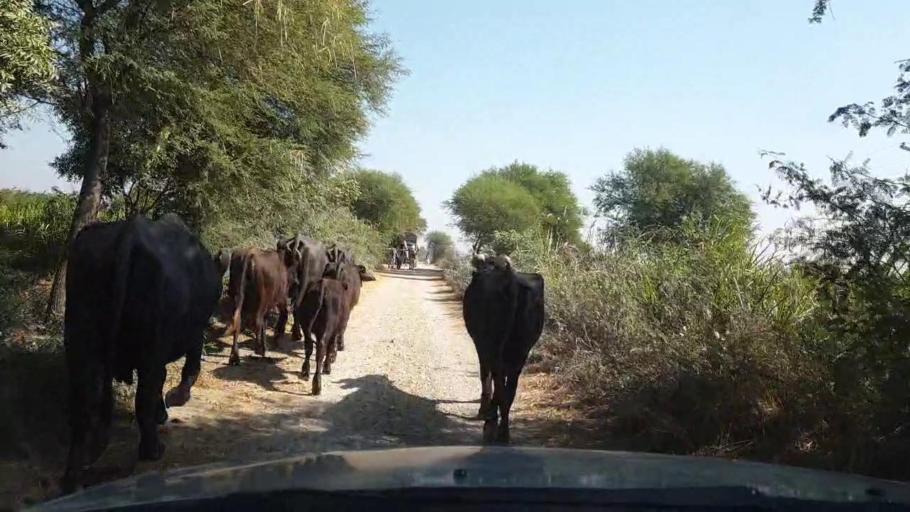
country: PK
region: Sindh
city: Tando Muhammad Khan
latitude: 24.9939
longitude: 68.5224
